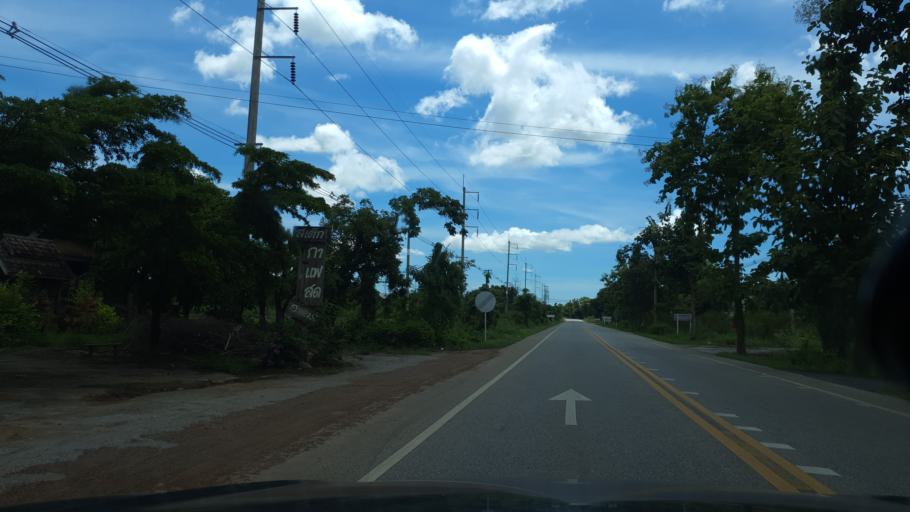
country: TH
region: Sukhothai
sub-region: Amphoe Si Satchanalai
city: Si Satchanalai
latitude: 17.5004
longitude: 99.7582
